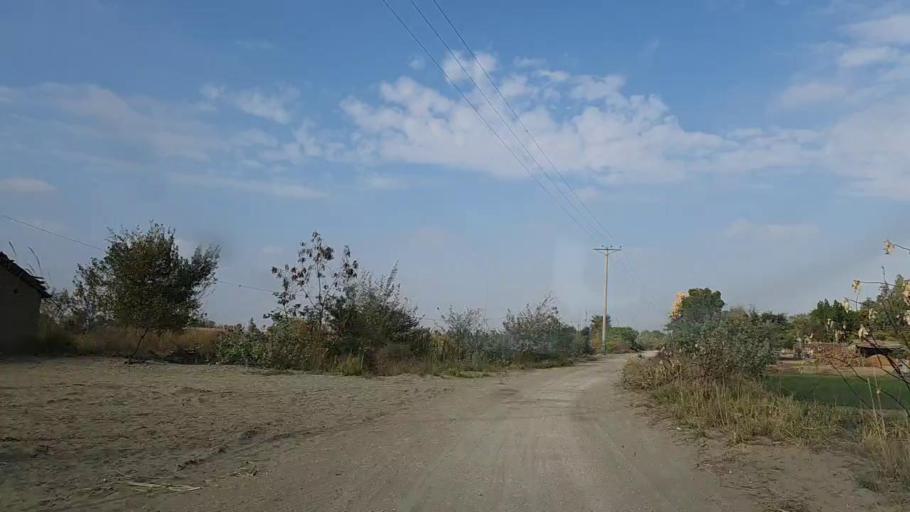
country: PK
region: Sindh
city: Sanghar
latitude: 26.2754
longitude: 69.0092
